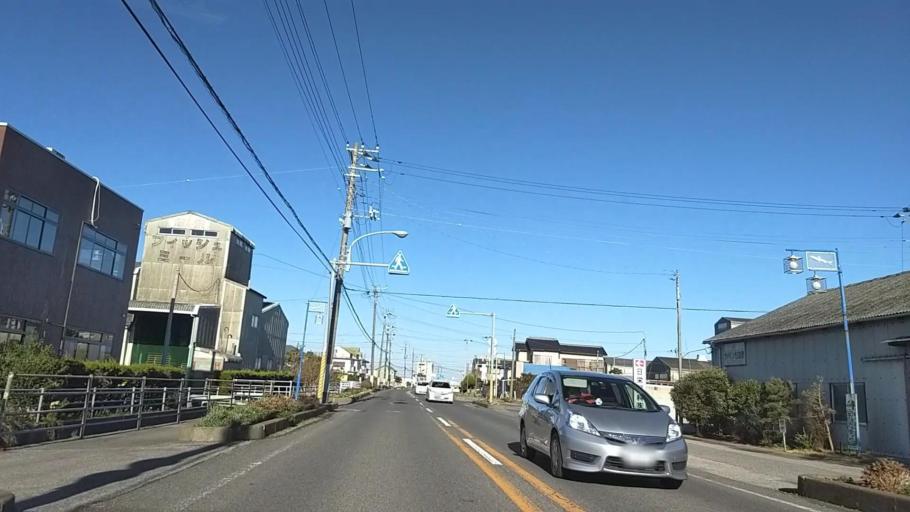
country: JP
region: Chiba
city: Naruto
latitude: 35.5349
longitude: 140.4525
